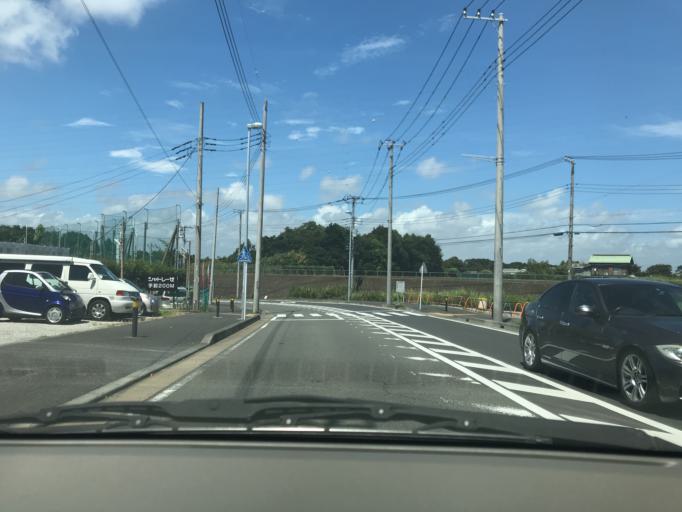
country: JP
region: Kanagawa
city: Fujisawa
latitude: 35.3668
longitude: 139.4601
